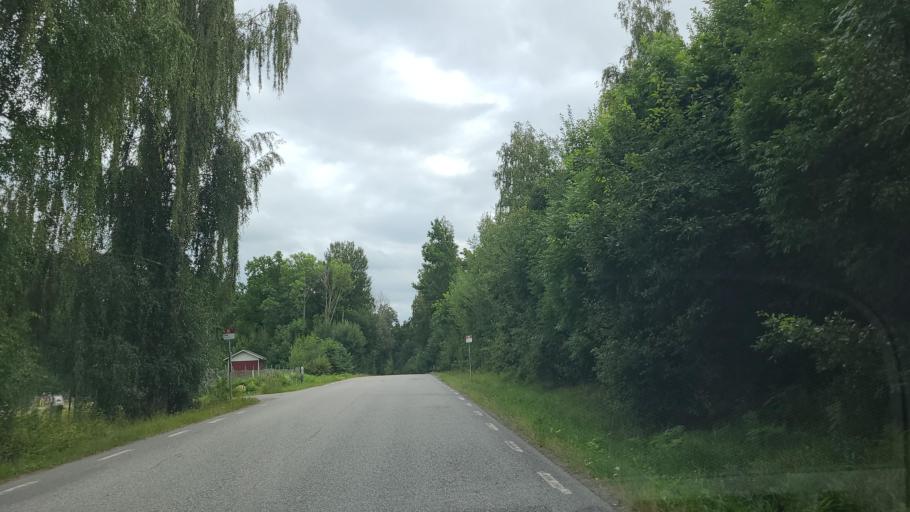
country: SE
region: Stockholm
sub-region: Upplands-Bro Kommun
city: Bro
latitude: 59.4993
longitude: 17.5673
